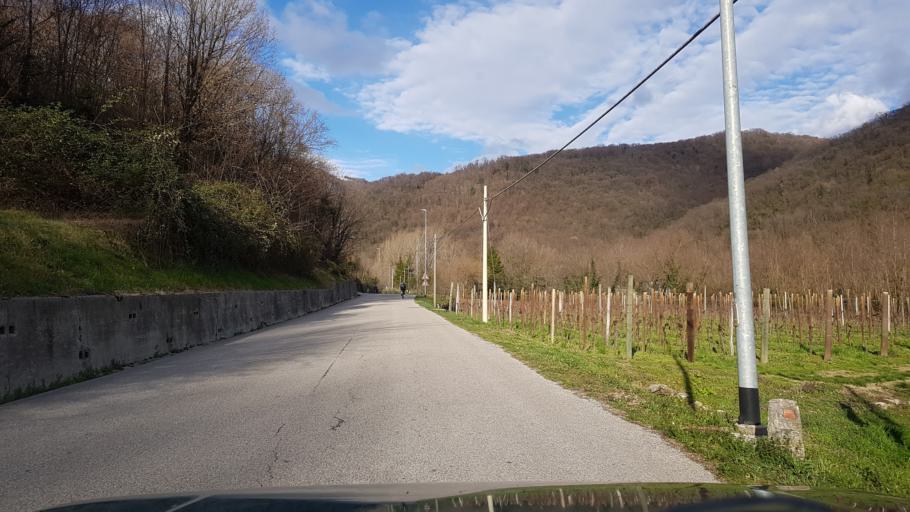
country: IT
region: Friuli Venezia Giulia
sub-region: Provincia di Udine
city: Faedis
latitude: 46.1602
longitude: 13.3541
